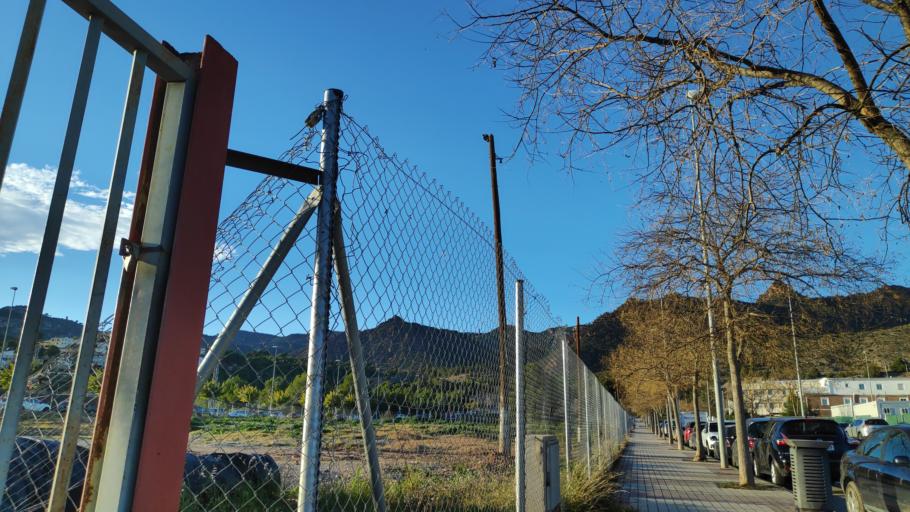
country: ES
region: Valencia
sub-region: Provincia de Castello
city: Benicassim
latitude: 40.0563
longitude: 0.0609
